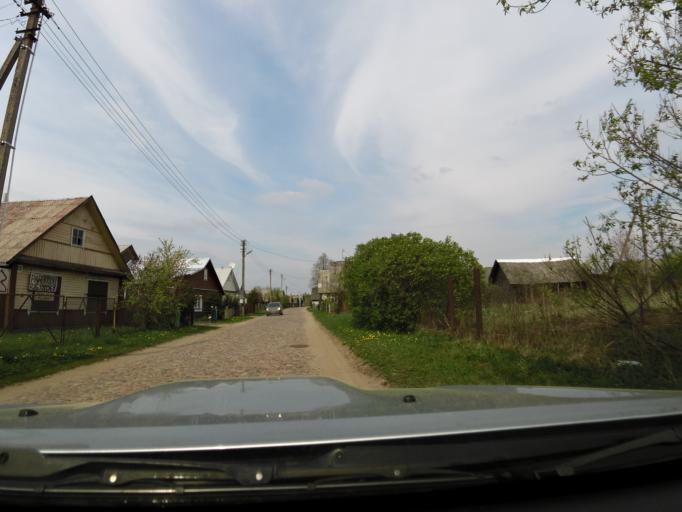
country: LT
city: Baltoji Voke
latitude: 54.4350
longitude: 25.1507
